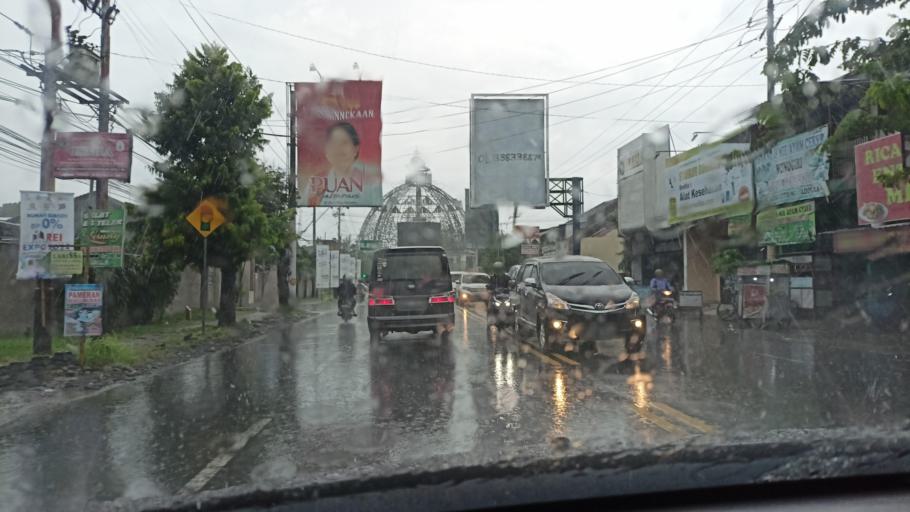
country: ID
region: Central Java
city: Colomadu
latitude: -7.5461
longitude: 110.7765
